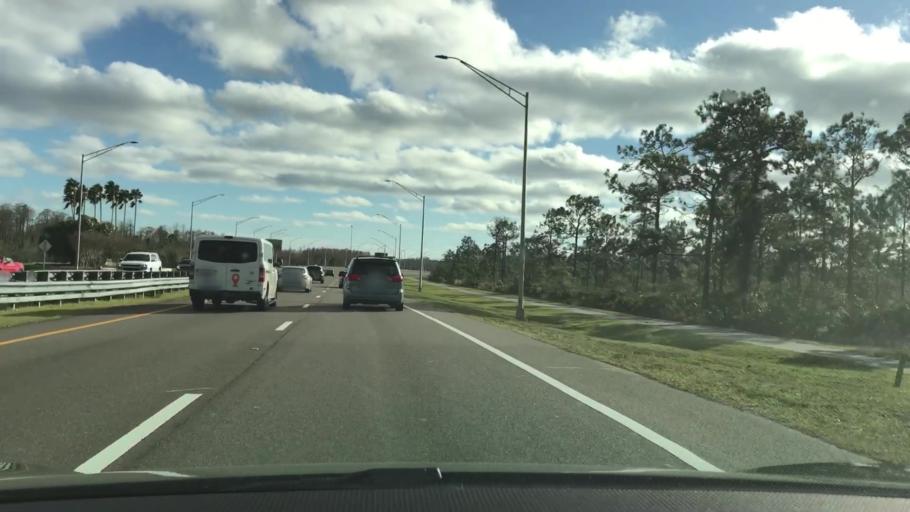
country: US
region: Florida
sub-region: Orange County
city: Taft
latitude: 28.4061
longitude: -81.3073
